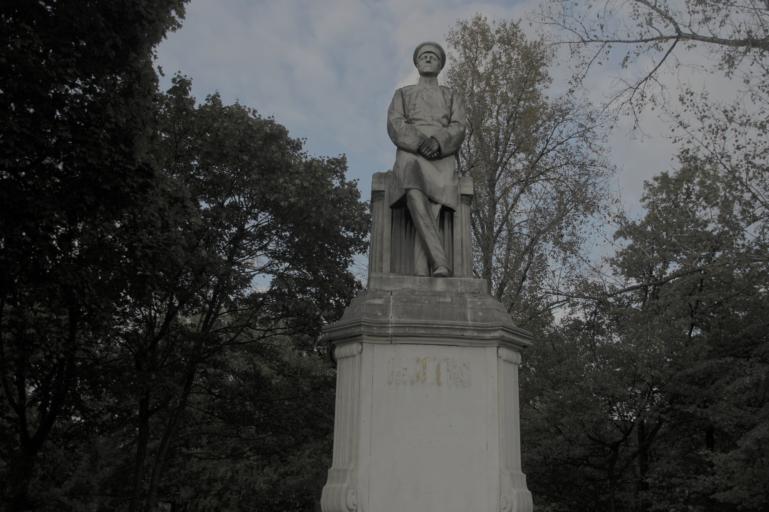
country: DE
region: Berlin
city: Hansaviertel
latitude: 52.5158
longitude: 13.3516
